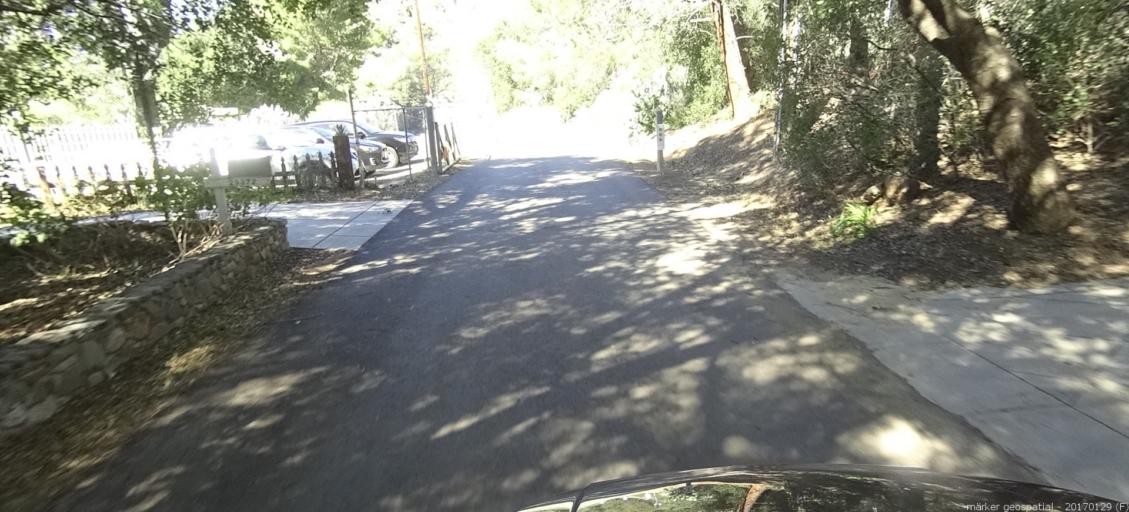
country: US
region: California
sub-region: Orange County
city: Portola Hills
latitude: 33.7098
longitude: -117.6177
